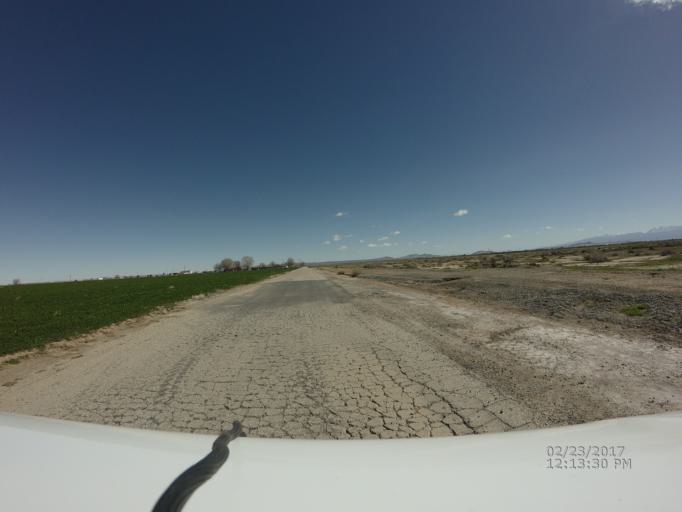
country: US
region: California
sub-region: Los Angeles County
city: Lancaster
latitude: 34.7414
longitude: -118.0026
